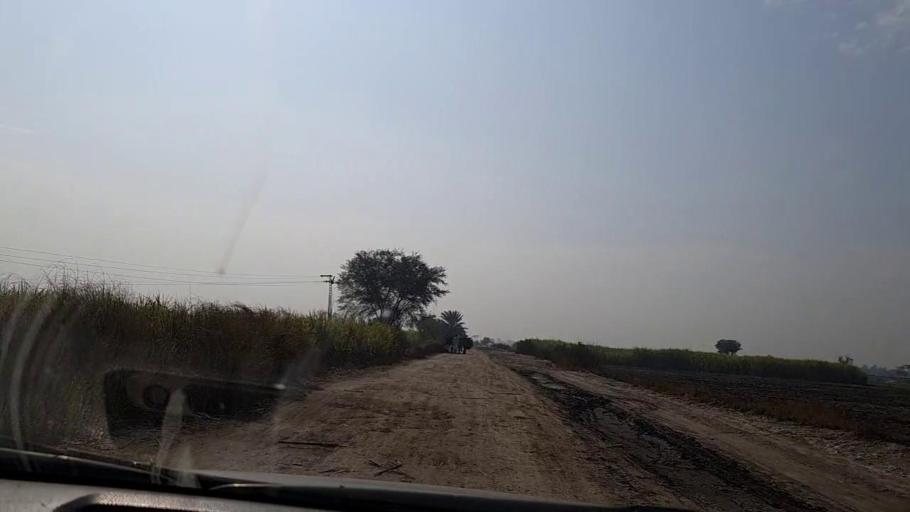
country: PK
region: Sindh
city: Daulatpur
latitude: 26.5511
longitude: 67.9819
